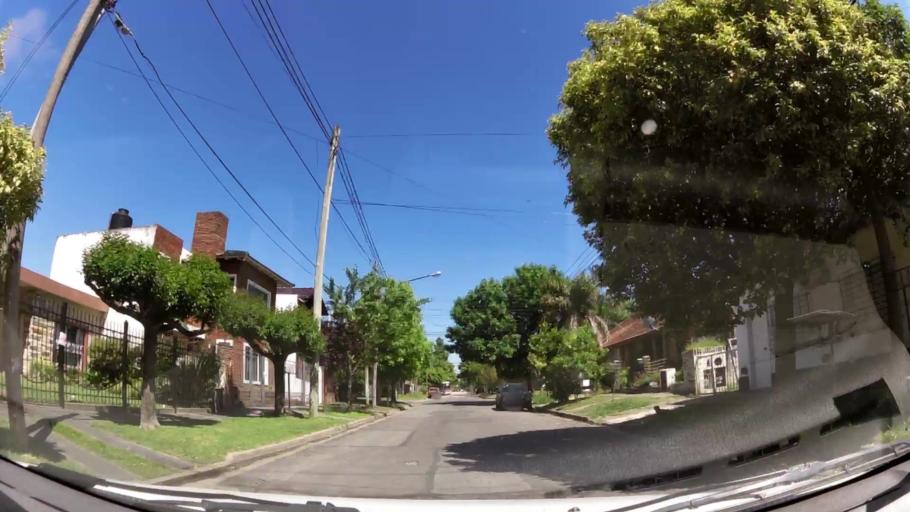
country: AR
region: Buenos Aires
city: Ituzaingo
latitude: -34.6625
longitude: -58.6571
